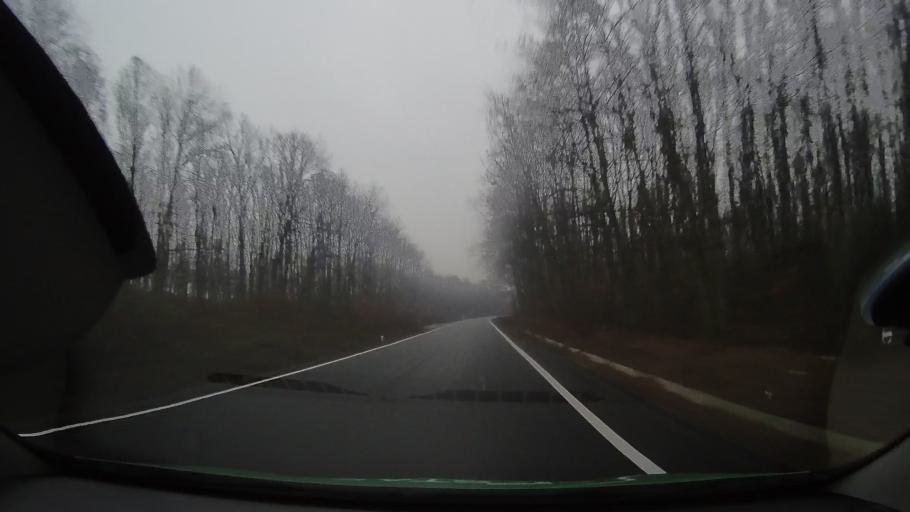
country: RO
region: Bihor
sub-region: Comuna Olcea
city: Olcea
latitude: 46.7009
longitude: 21.9642
